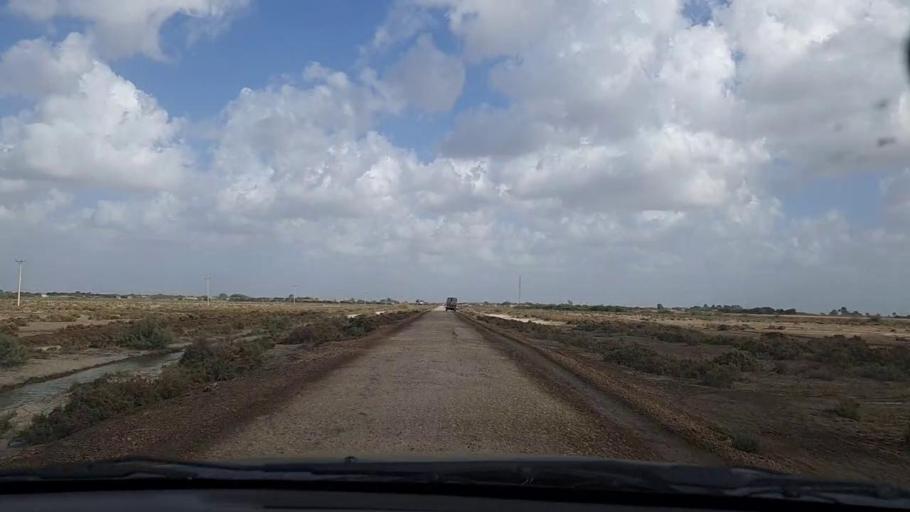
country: PK
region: Sindh
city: Keti Bandar
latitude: 24.1055
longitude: 67.5901
